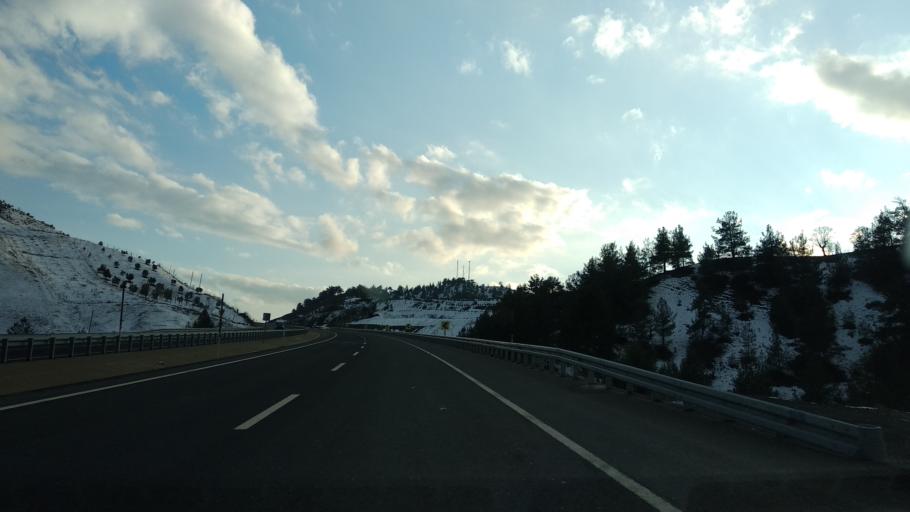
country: TR
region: Kahramanmaras
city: Yenicekale
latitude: 37.7287
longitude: 36.6979
